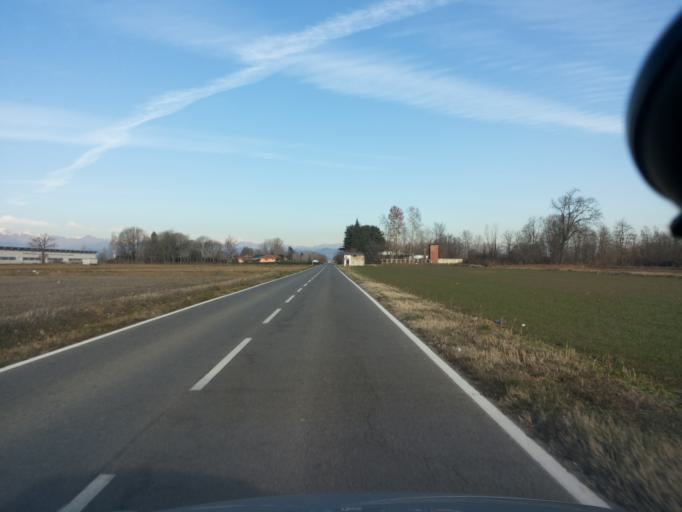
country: IT
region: Piedmont
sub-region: Provincia di Vercelli
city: Arborio
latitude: 45.5059
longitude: 8.3886
